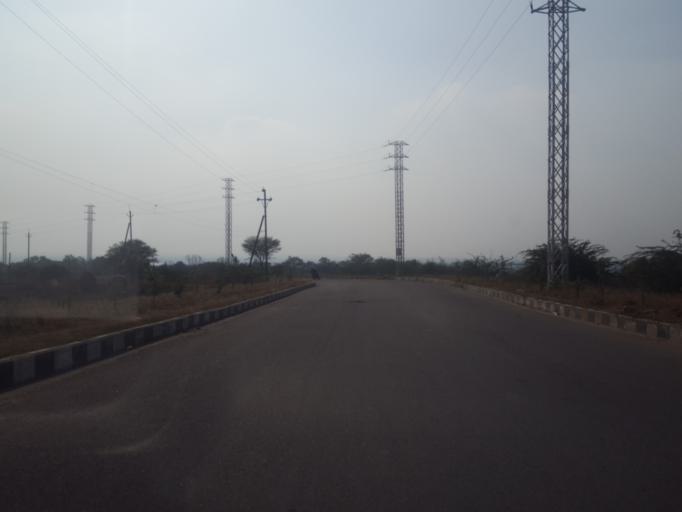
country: IN
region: Telangana
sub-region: Medak
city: Serilingampalle
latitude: 17.4034
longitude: 78.3123
